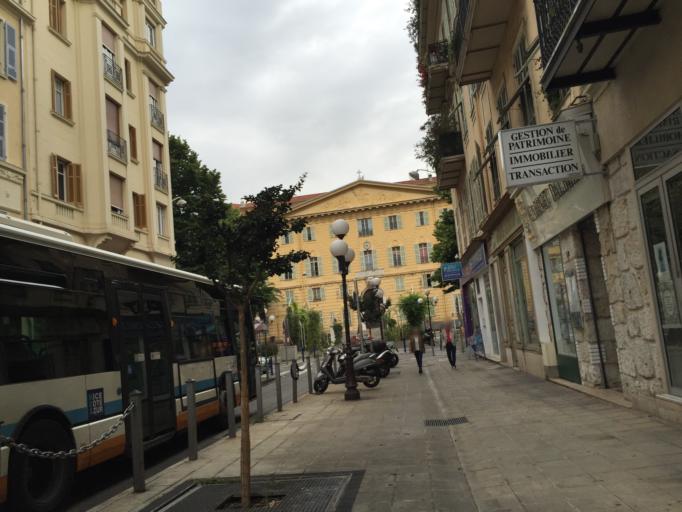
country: FR
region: Provence-Alpes-Cote d'Azur
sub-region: Departement des Alpes-Maritimes
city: Nice
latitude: 43.7023
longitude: 7.2763
